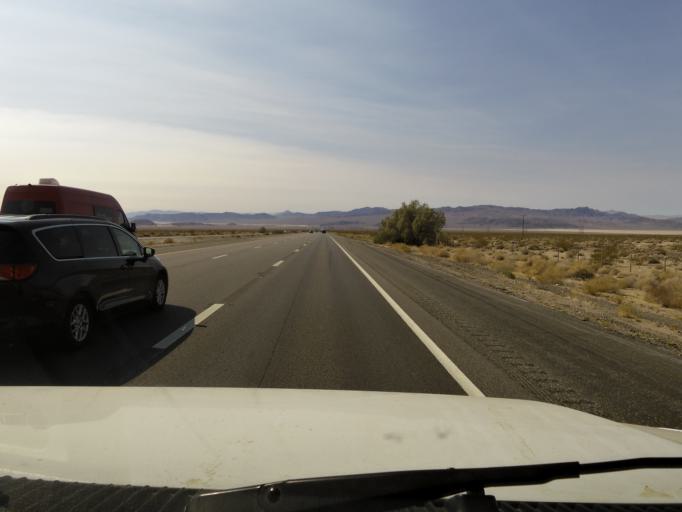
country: US
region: Nevada
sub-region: Clark County
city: Sandy Valley
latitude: 35.3297
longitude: -115.9738
